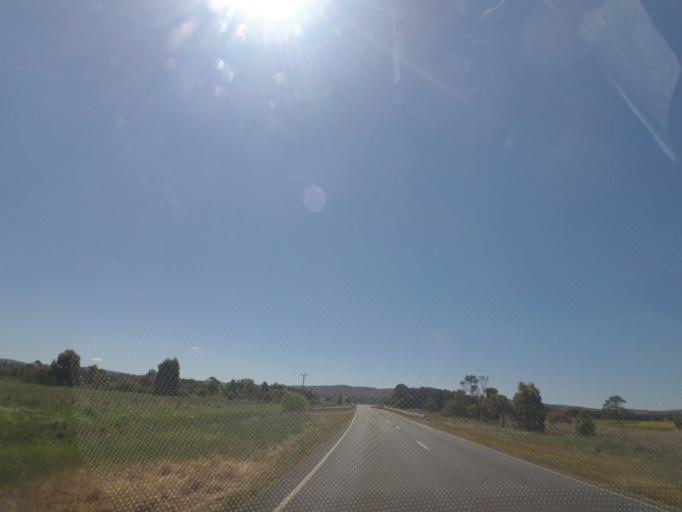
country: AU
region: Victoria
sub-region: Hume
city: Sunbury
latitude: -37.2620
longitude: 144.7366
